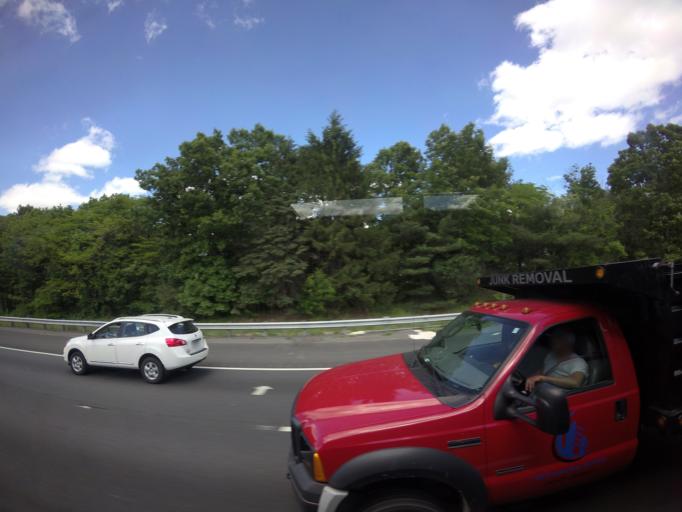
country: US
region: Massachusetts
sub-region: Middlesex County
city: Wilmington
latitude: 42.5708
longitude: -71.1476
